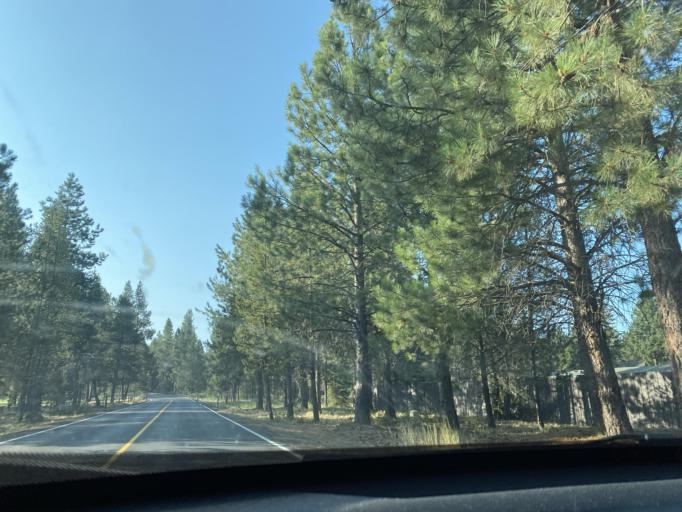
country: US
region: Oregon
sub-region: Deschutes County
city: Sunriver
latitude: 43.8813
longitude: -121.4383
